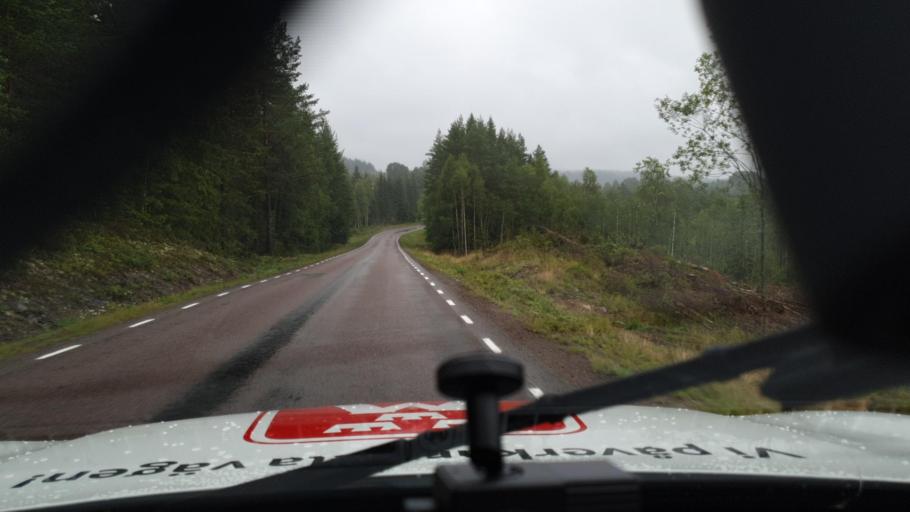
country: SE
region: Vaermland
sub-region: Arvika Kommun
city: Arvika
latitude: 59.9500
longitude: 12.6976
